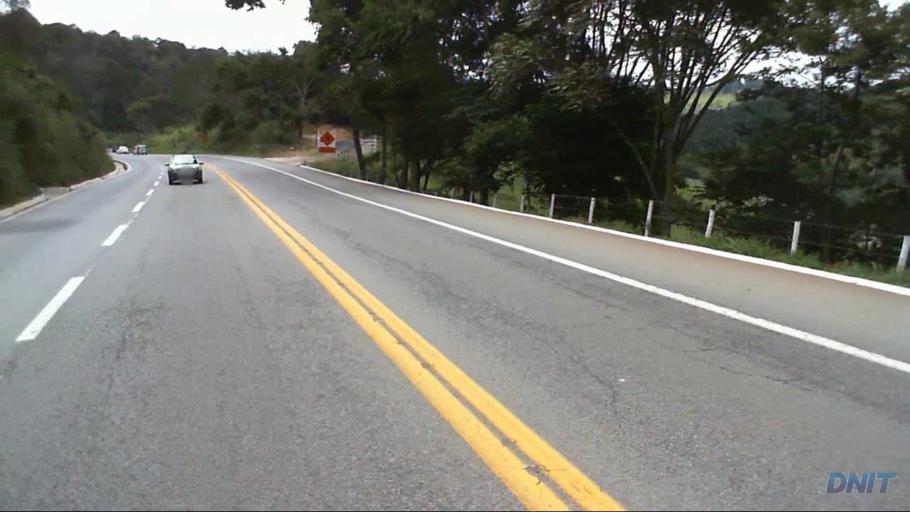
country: BR
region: Minas Gerais
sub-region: Caete
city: Caete
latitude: -19.7528
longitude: -43.6296
